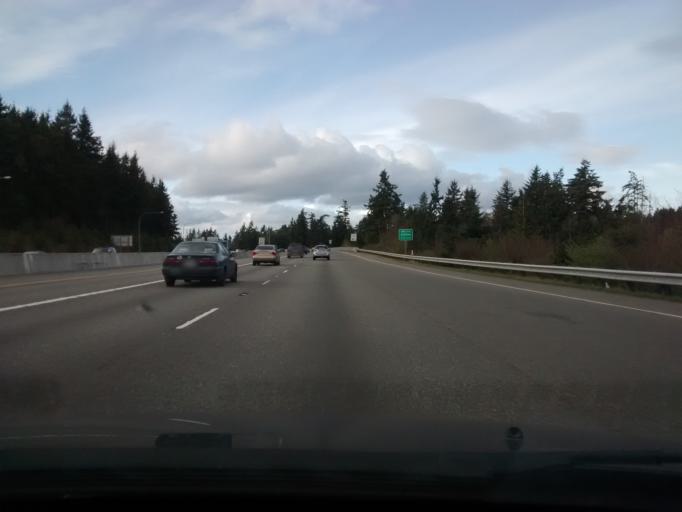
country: US
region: Washington
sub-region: Pierce County
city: Wollochet
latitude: 47.2838
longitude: -122.5604
